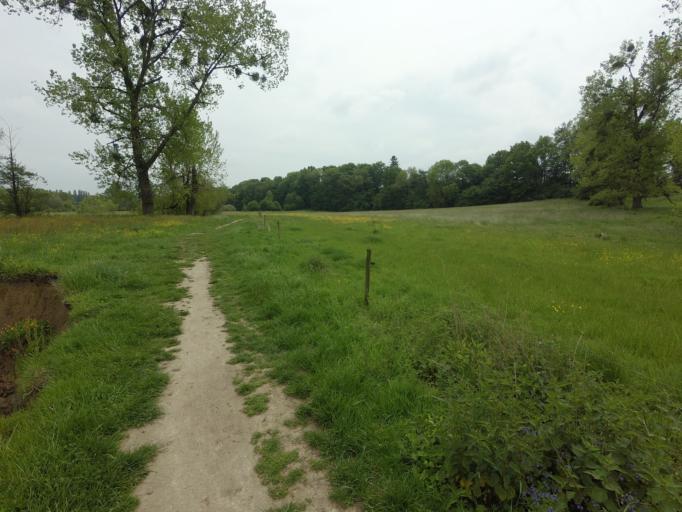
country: BE
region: Wallonia
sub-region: Province de Liege
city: Plombieres
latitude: 50.7584
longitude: 5.9313
